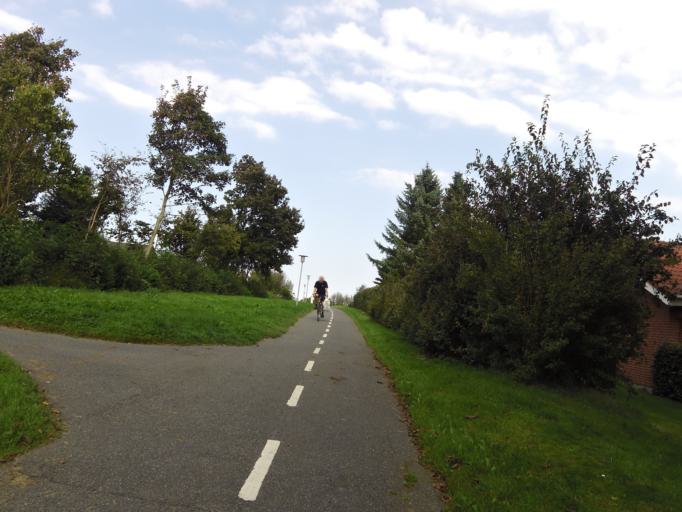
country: DK
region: South Denmark
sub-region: Vejen Kommune
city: Vejen
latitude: 55.4640
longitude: 9.1287
